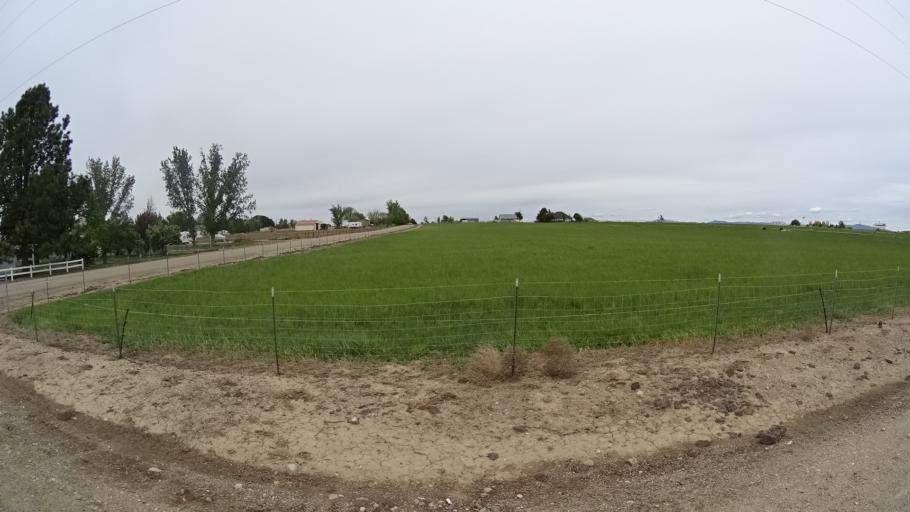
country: US
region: Idaho
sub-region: Ada County
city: Kuna
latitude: 43.4883
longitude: -116.2990
